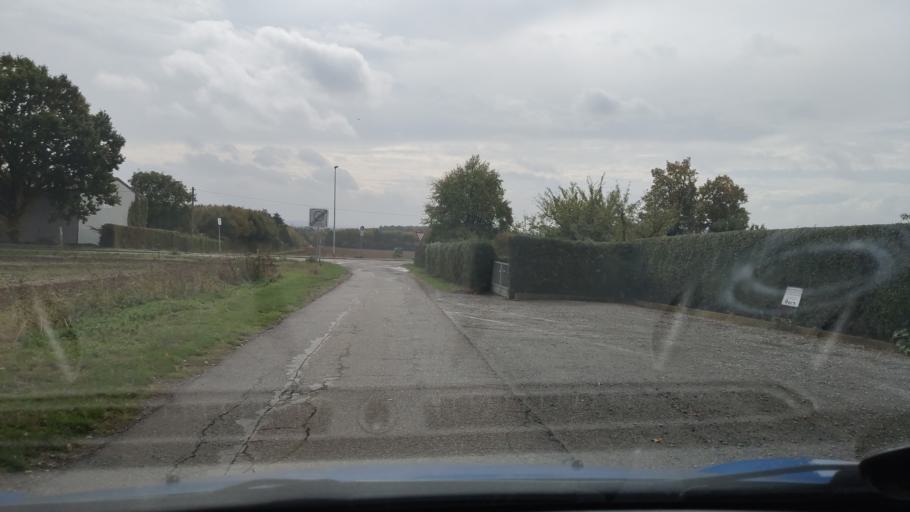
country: DE
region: Lower Saxony
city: Ronnenberg
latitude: 52.3711
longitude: 9.6570
